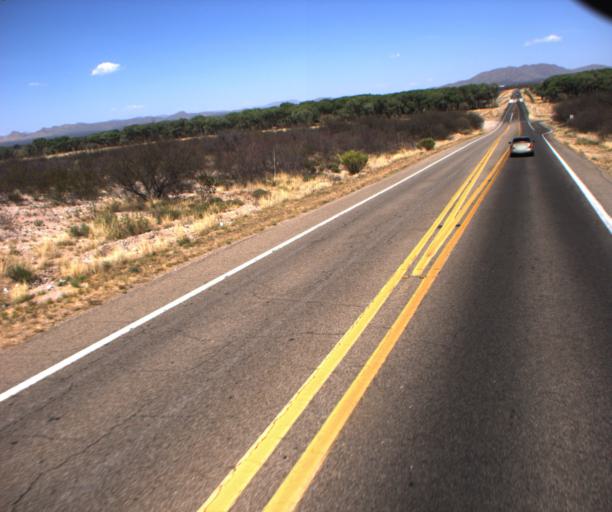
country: US
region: Arizona
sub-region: Cochise County
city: Sierra Vista Southeast
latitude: 31.5496
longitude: -110.1454
